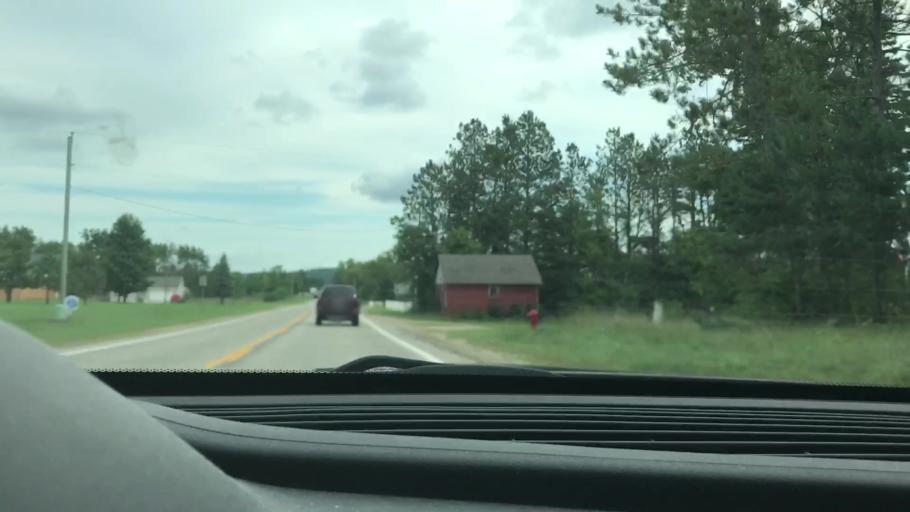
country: US
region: Michigan
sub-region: Antrim County
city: Mancelona
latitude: 44.9022
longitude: -85.0807
